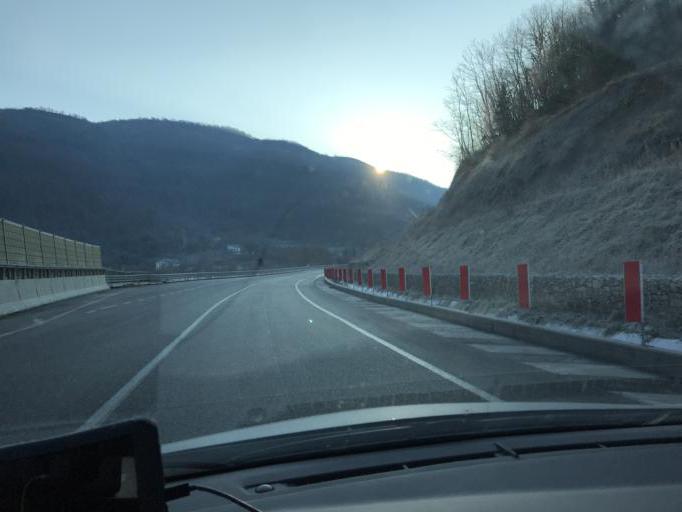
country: IT
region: Latium
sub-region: Provincia di Rieti
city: Cittaducale
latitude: 42.3512
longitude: 12.9601
